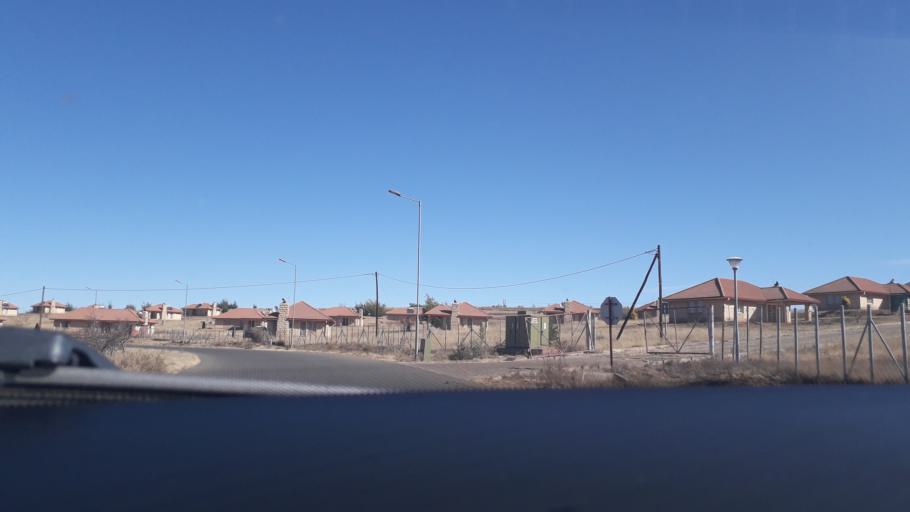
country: LS
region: Berea
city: Teyateyaneng
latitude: -29.3269
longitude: 27.7730
